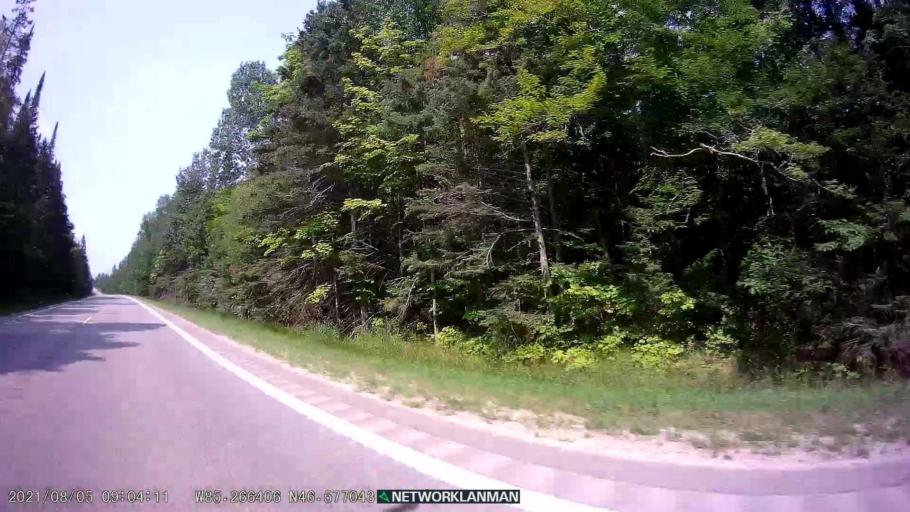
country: US
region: Michigan
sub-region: Luce County
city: Newberry
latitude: 46.5769
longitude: -85.2667
